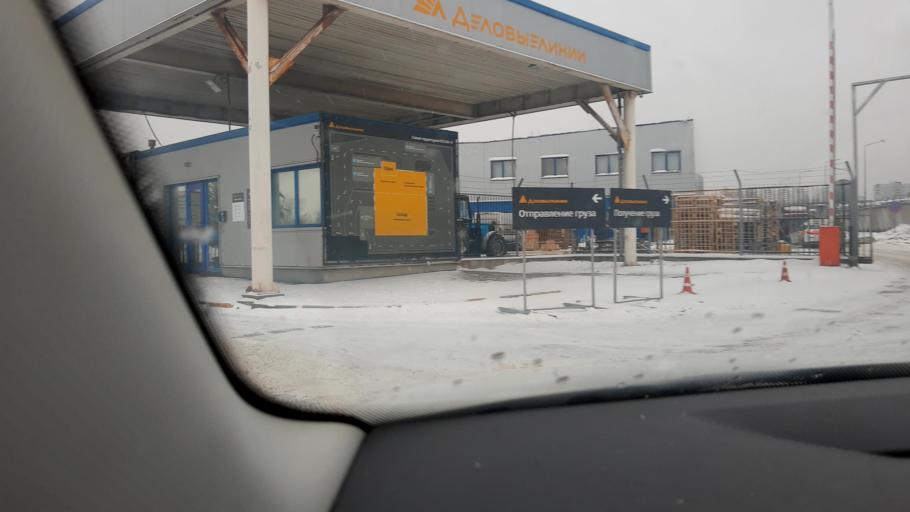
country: RU
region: Moskovskaya
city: Biryulevo Zapadnoye
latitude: 55.6011
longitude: 37.6434
